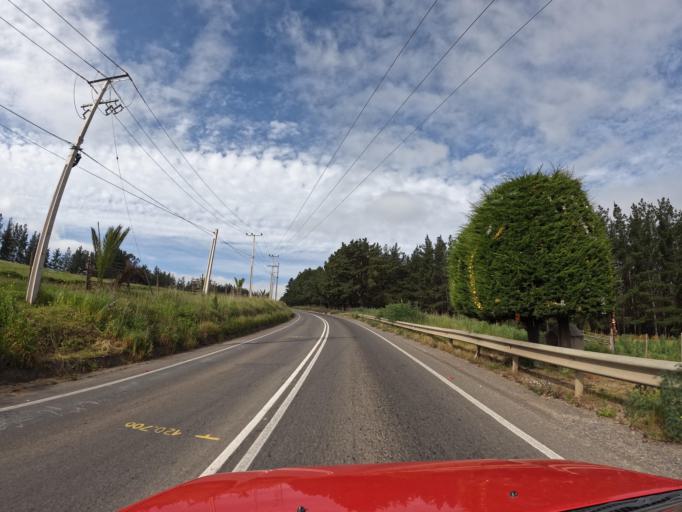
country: CL
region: O'Higgins
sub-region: Provincia de Colchagua
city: Santa Cruz
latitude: -34.3680
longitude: -71.9567
